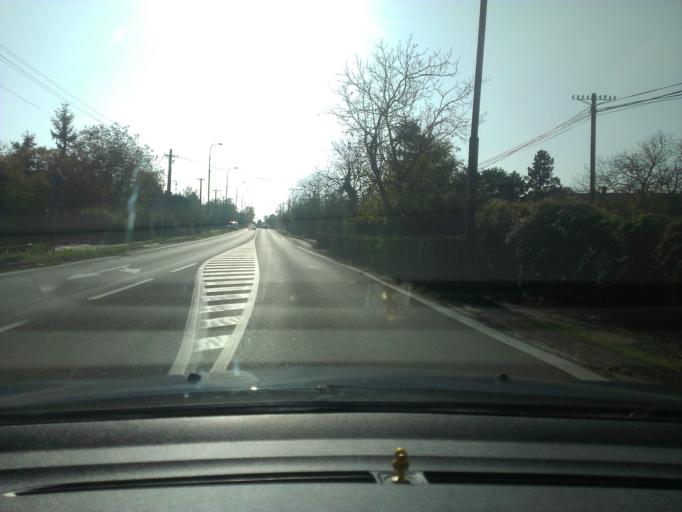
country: SK
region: Nitriansky
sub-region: Okres Komarno
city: Hurbanovo
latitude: 47.8530
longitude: 18.1721
